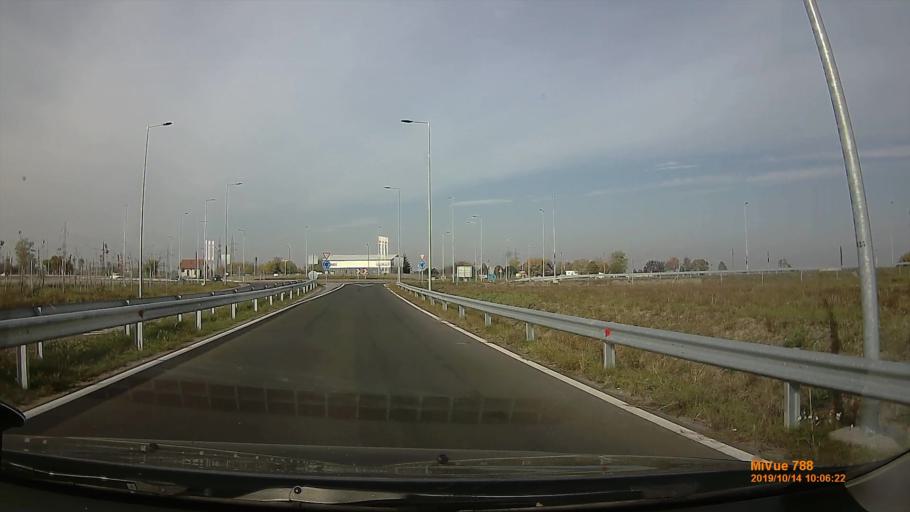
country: HU
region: Pest
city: Cegled
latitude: 47.1942
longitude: 19.8138
